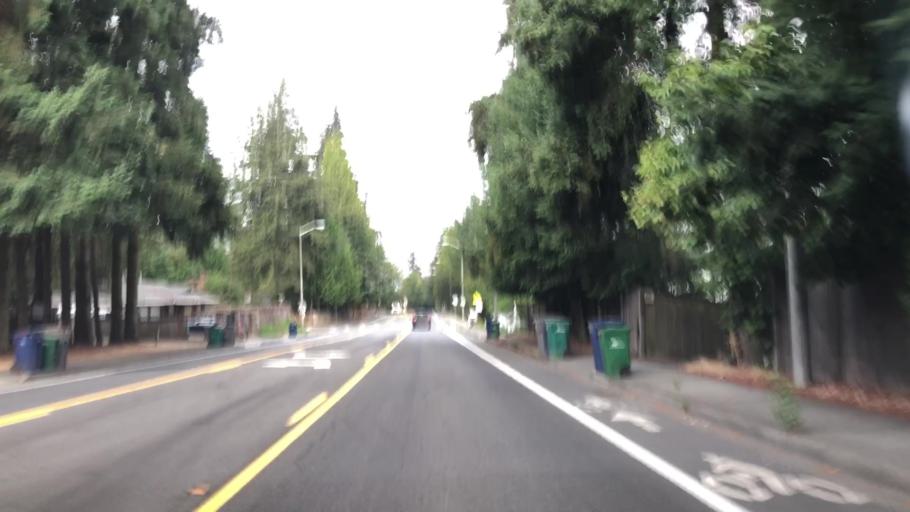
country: US
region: Washington
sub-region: King County
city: Kirkland
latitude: 47.6682
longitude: -122.1789
